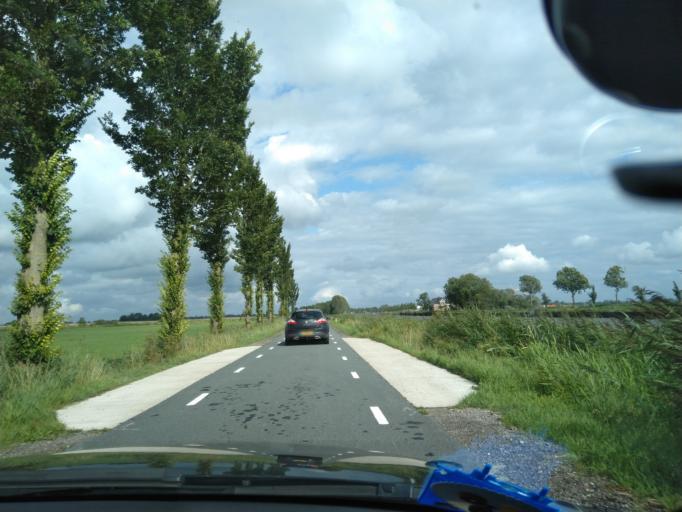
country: NL
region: Groningen
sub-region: Gemeente Zuidhorn
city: Noordhorn
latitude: 53.2538
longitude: 6.3559
